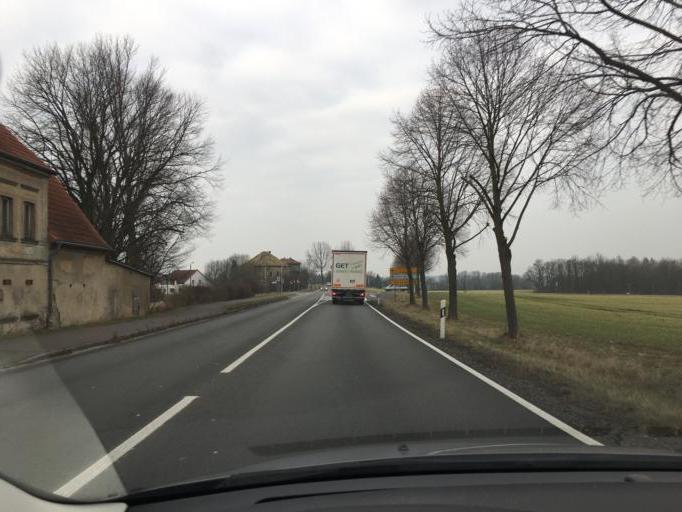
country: DE
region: Saxony
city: Regis-Breitingen
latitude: 51.0921
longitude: 12.4720
